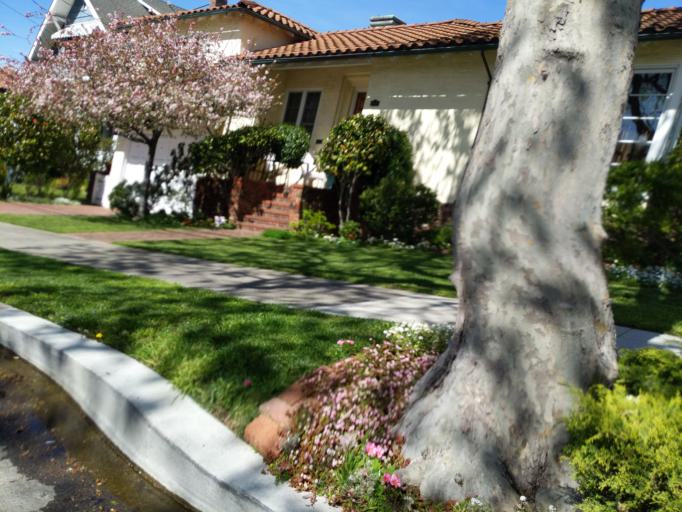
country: US
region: California
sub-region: Alameda County
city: Alameda
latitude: 37.7599
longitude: -122.2343
